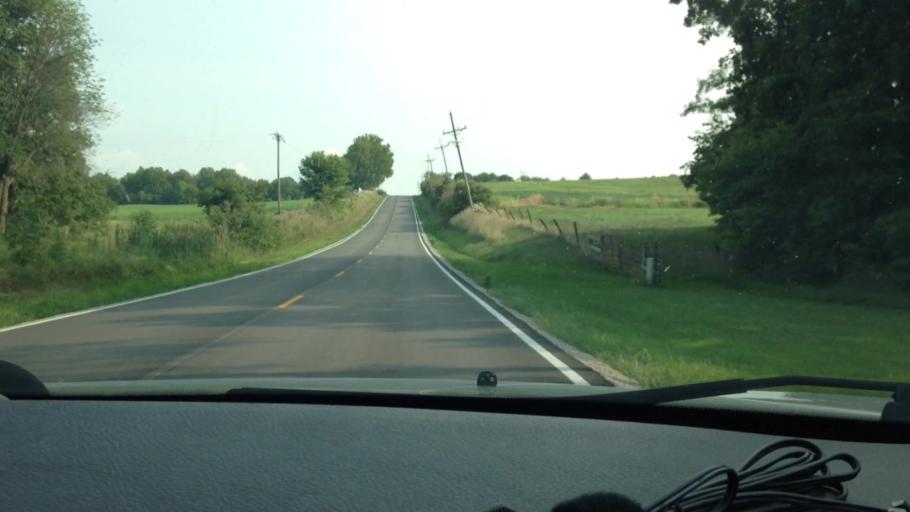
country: US
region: Missouri
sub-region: Platte County
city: Platte City
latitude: 39.4235
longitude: -94.7799
